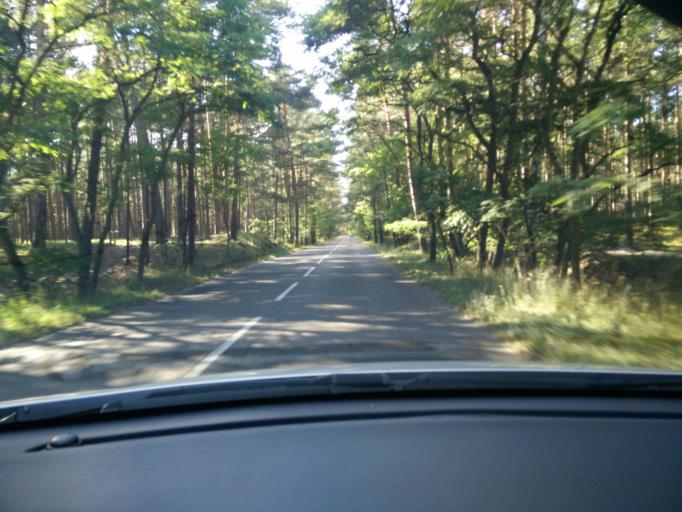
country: PL
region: Pomeranian Voivodeship
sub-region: Powiat pucki
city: Hel
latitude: 54.6328
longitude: 18.7844
